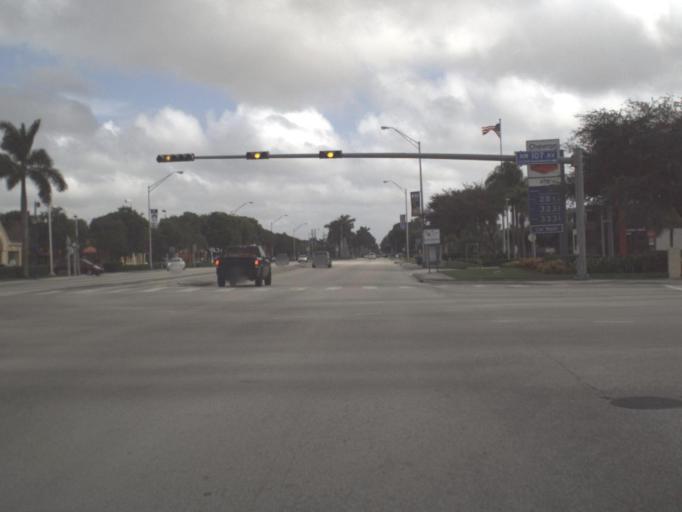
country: US
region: Florida
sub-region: Miami-Dade County
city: Doral
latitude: 25.8116
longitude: -80.3697
